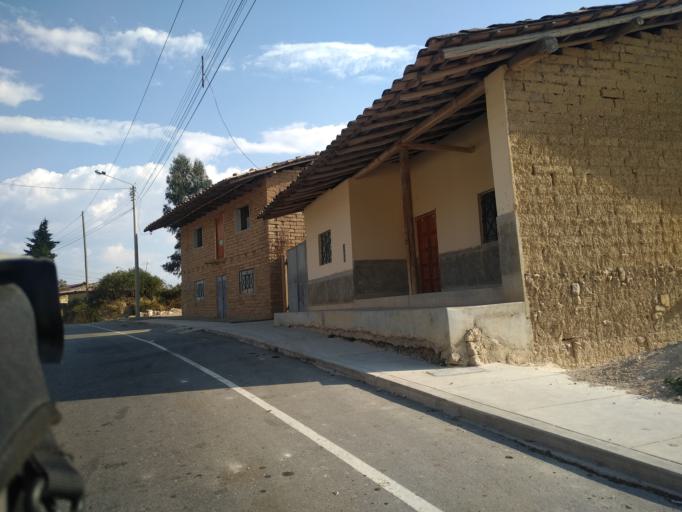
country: PE
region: Cajamarca
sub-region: San Marcos
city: San Marcos
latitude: -7.3846
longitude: -78.1255
